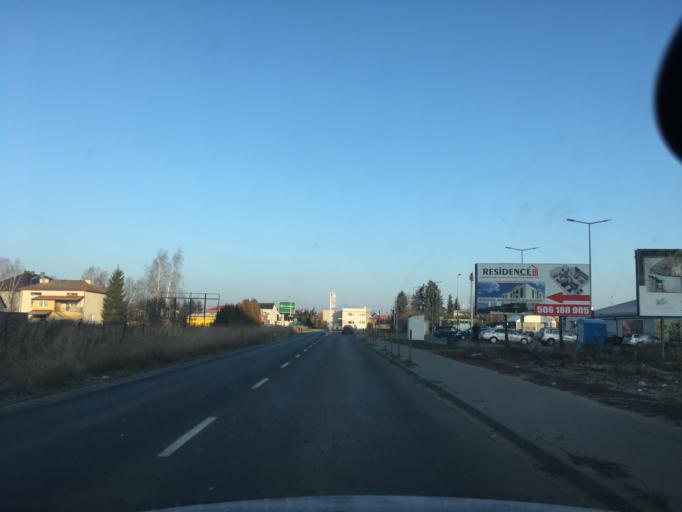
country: PL
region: Masovian Voivodeship
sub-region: Powiat piaseczynski
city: Piaseczno
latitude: 52.0810
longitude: 21.0082
